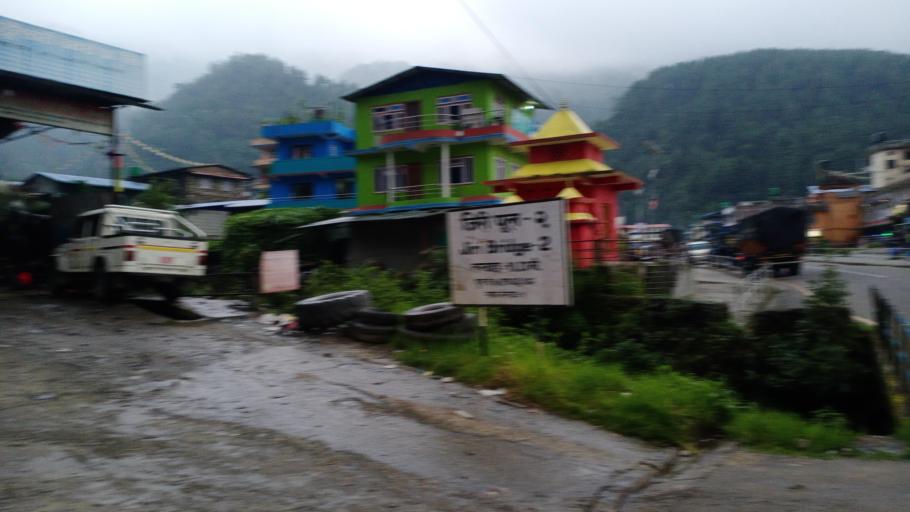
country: NP
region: Central Region
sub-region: Janakpur Zone
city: Ramechhap
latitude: 27.6367
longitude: 86.2289
